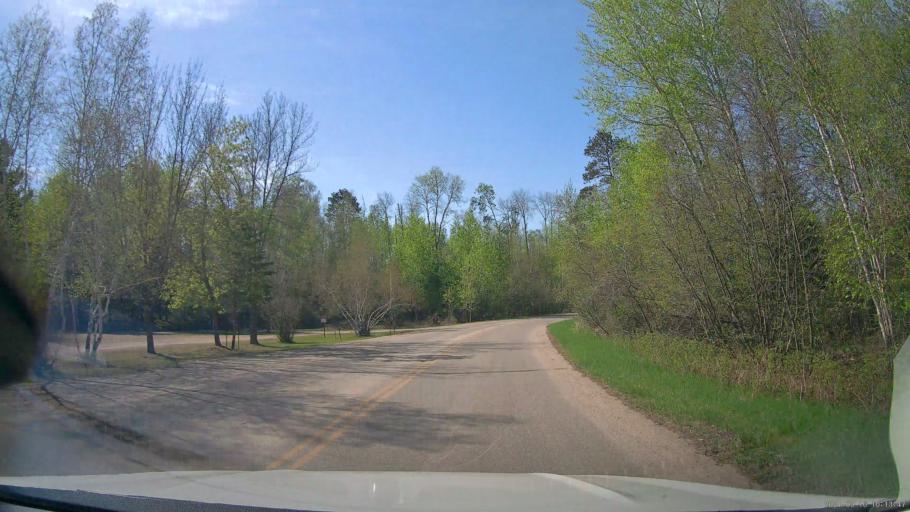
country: US
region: Minnesota
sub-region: Hubbard County
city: Park Rapids
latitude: 46.9854
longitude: -94.9488
